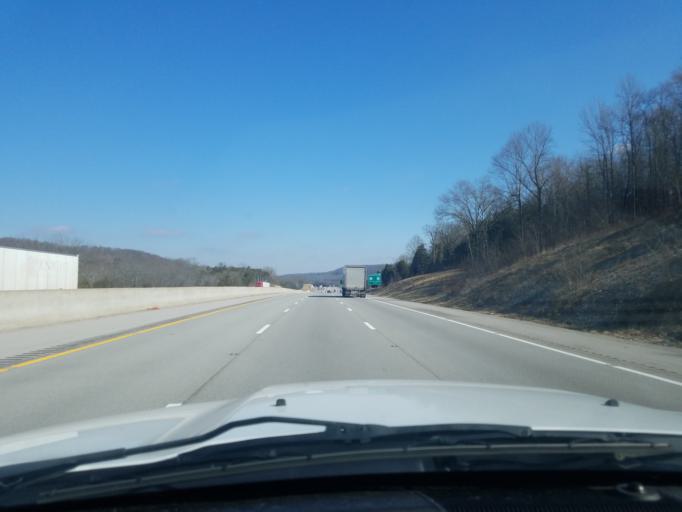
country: US
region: Kentucky
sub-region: Hart County
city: Horse Cave
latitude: 37.1830
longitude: -85.9479
